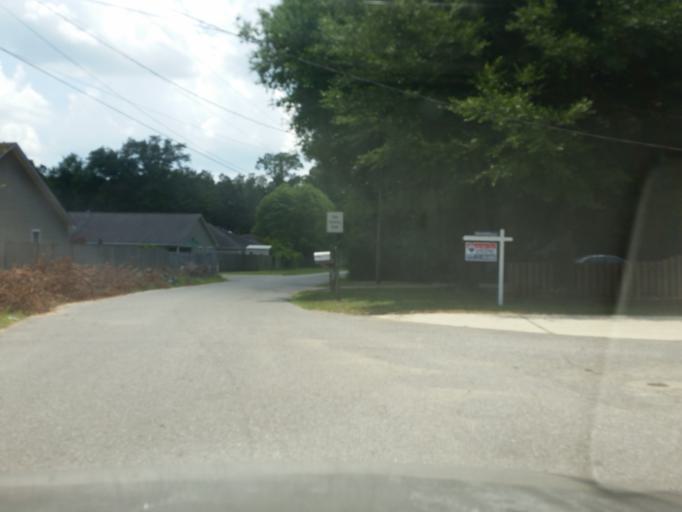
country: US
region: Florida
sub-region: Escambia County
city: Ferry Pass
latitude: 30.5145
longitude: -87.2000
